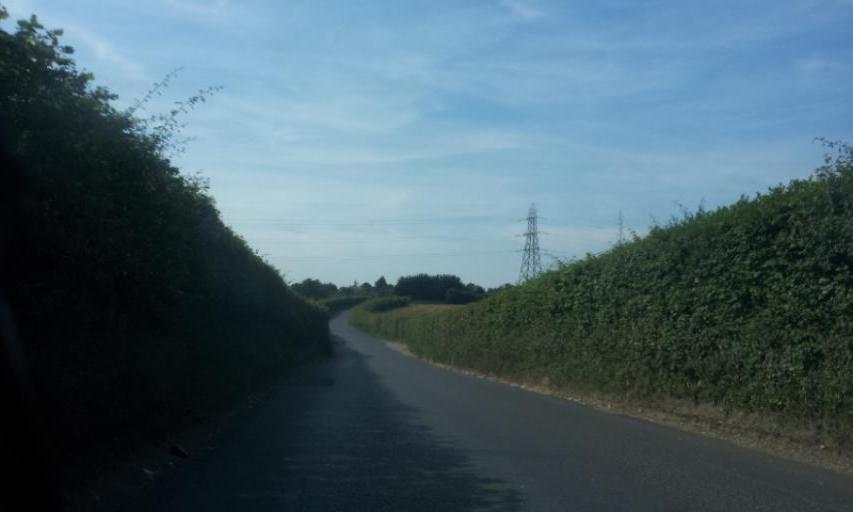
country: GB
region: England
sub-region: Kent
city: Newington
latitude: 51.3258
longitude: 0.6907
